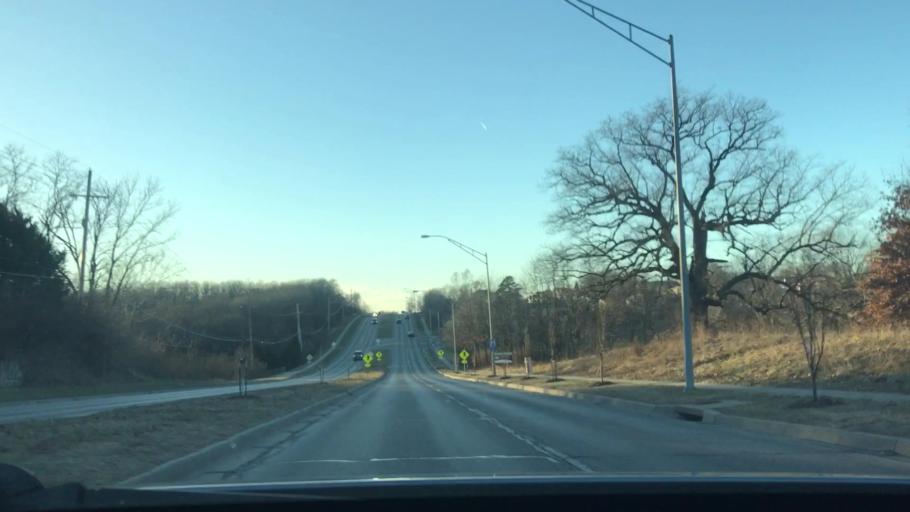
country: US
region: Missouri
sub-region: Platte County
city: Riverside
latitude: 39.2465
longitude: -94.6160
